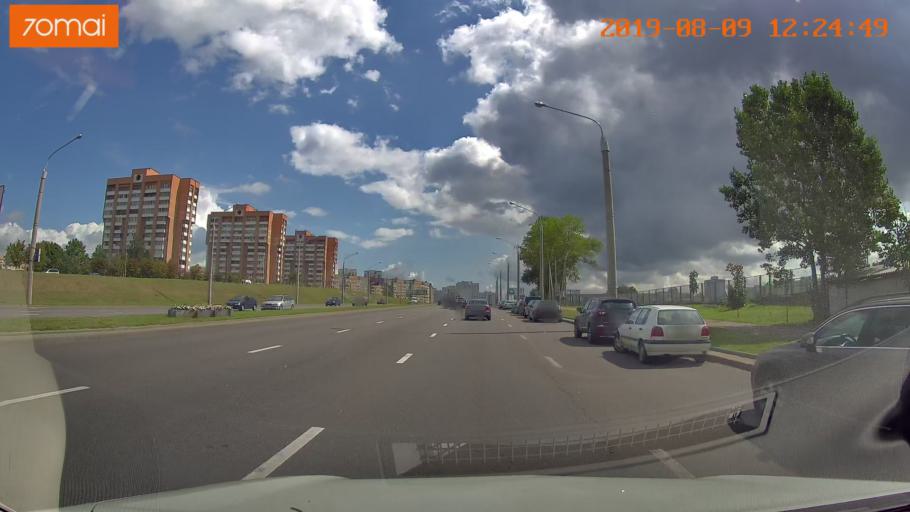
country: BY
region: Minsk
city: Novoye Medvezhino
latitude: 53.9296
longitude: 27.4908
